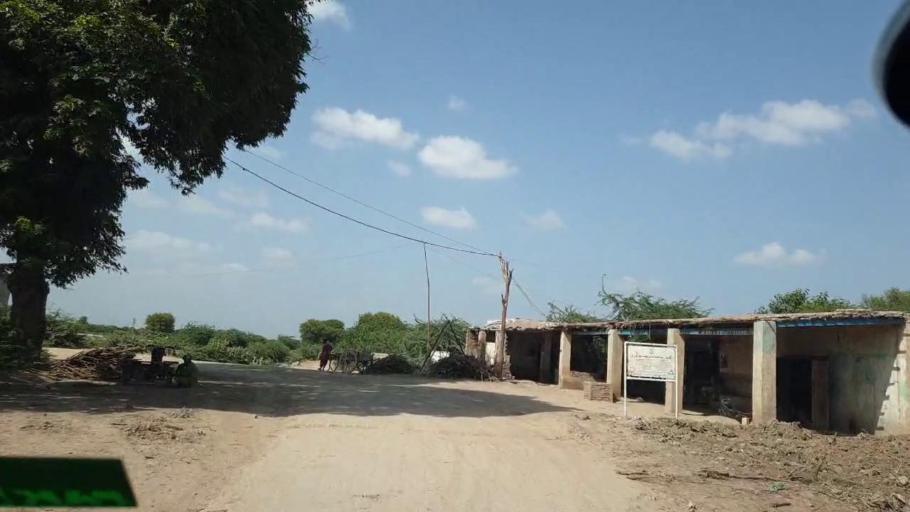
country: PK
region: Sindh
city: Naukot
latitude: 24.6429
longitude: 69.2274
